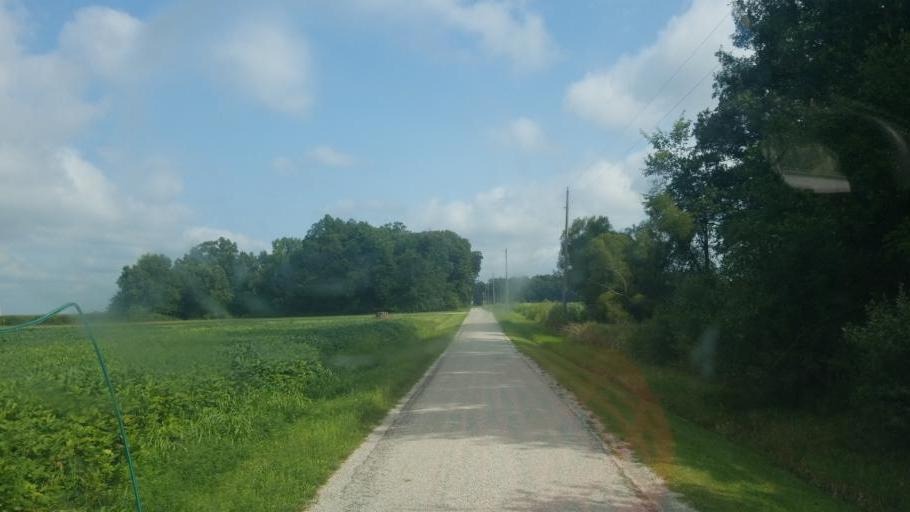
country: US
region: Ohio
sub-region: Marion County
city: Marion
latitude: 40.5715
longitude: -83.0053
